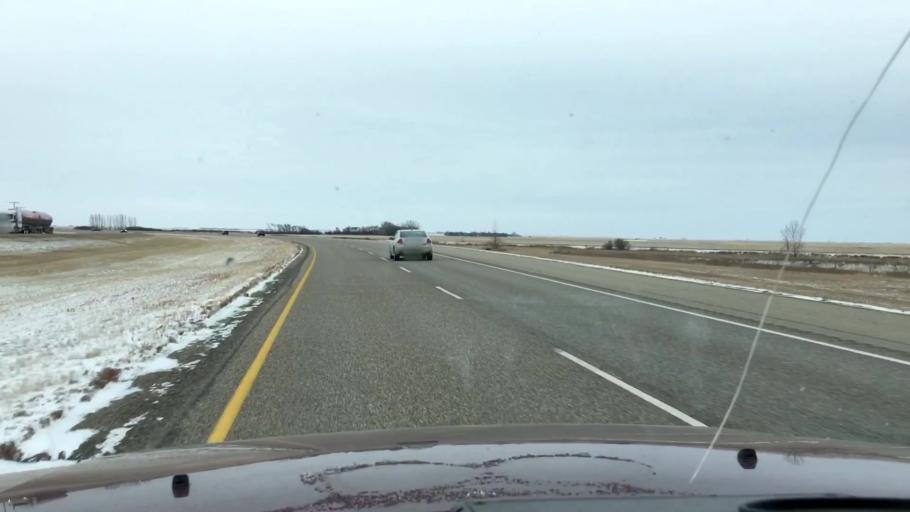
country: CA
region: Saskatchewan
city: Watrous
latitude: 51.1479
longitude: -105.9071
